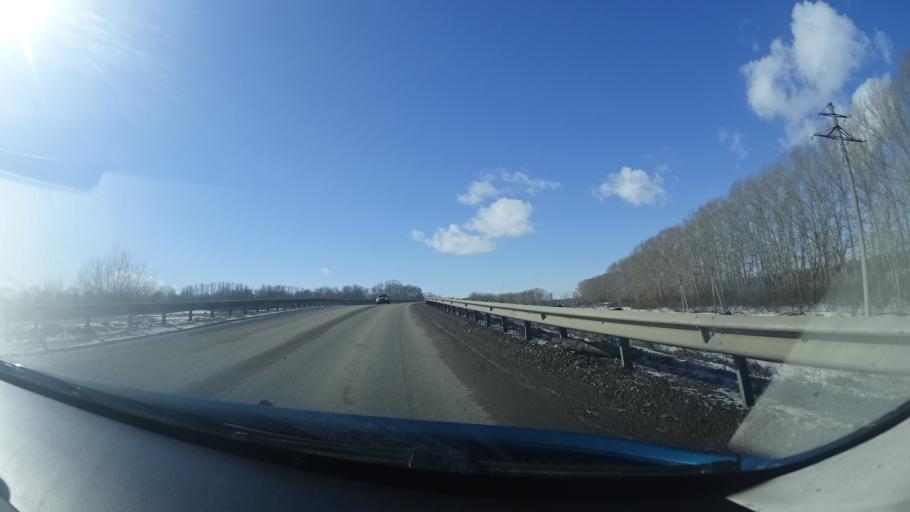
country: RU
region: Bashkortostan
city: Ufa
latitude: 54.6113
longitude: 55.8865
